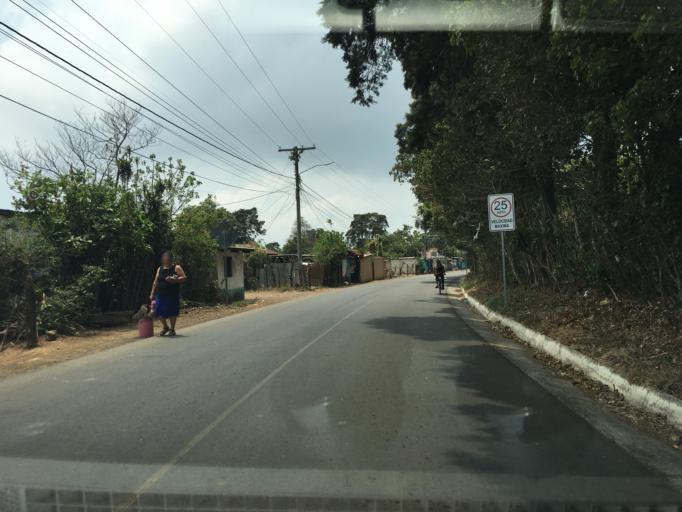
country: GT
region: Escuintla
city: San Vicente Pacaya
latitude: 14.3449
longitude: -90.5705
